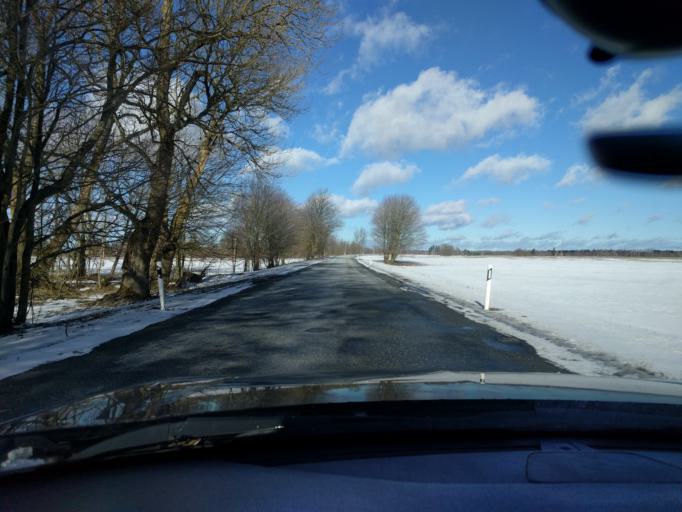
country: EE
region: Harju
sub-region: Raasiku vald
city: Raasiku
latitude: 59.3471
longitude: 25.1481
